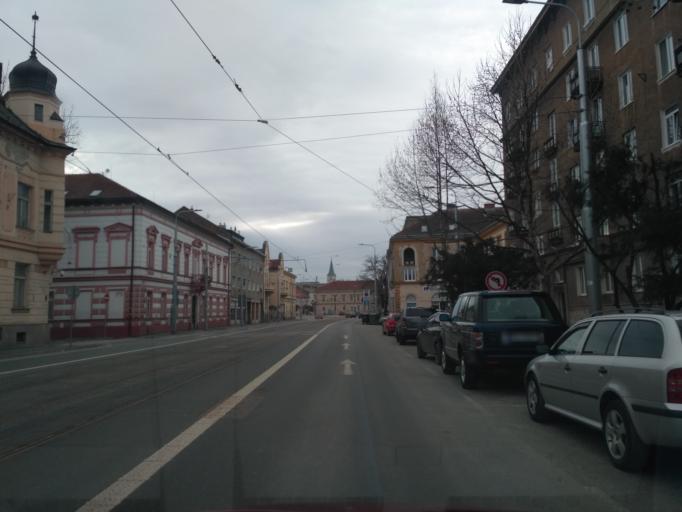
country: SK
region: Kosicky
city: Kosice
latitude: 48.7289
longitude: 21.2524
